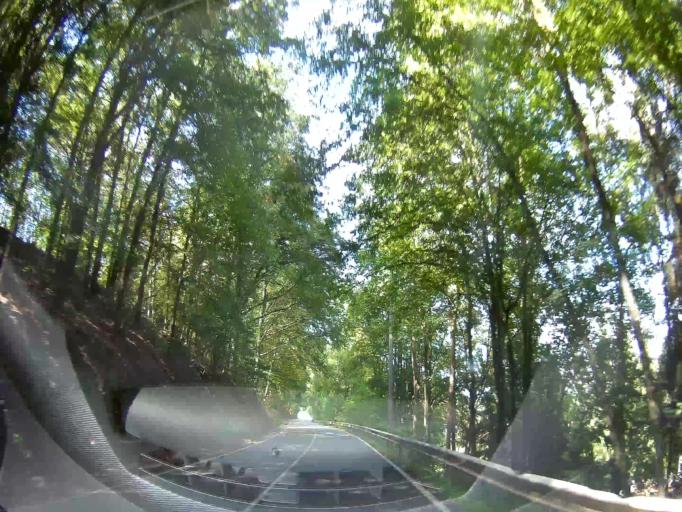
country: BE
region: Wallonia
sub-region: Province du Luxembourg
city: La Roche-en-Ardenne
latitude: 50.1943
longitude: 5.5392
